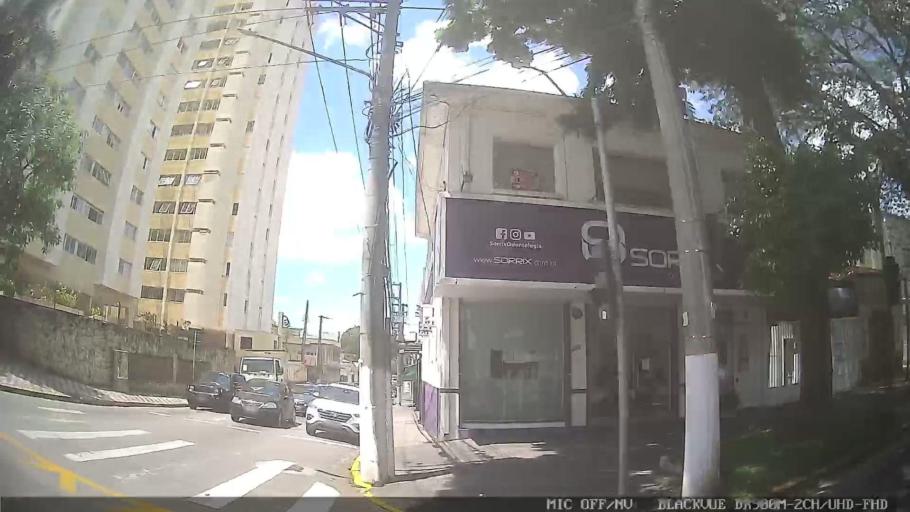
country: BR
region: Sao Paulo
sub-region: Jacarei
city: Jacarei
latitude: -23.3065
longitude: -45.9733
